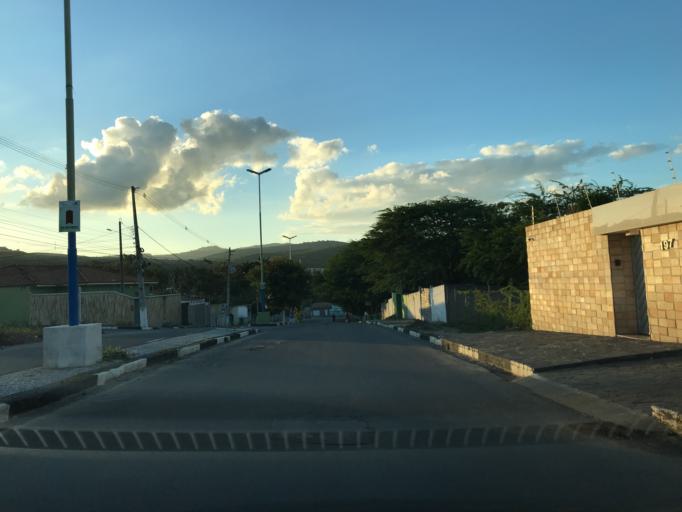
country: BR
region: Pernambuco
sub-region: Bezerros
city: Bezerros
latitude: -8.2403
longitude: -35.7603
